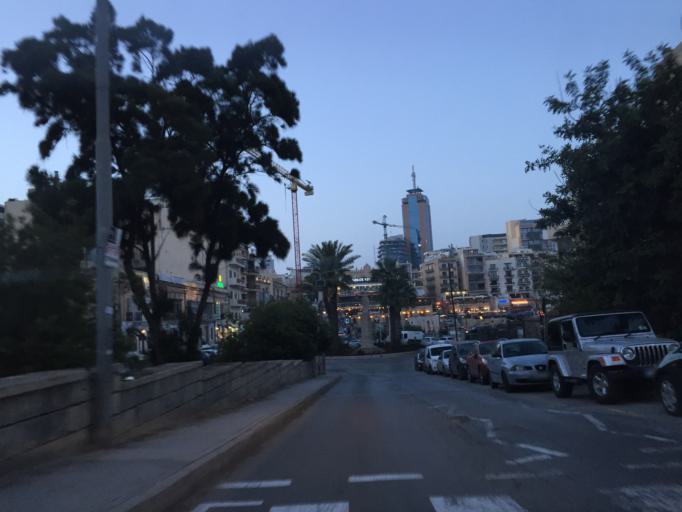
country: MT
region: Saint Julian
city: San Giljan
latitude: 35.9181
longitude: 14.4894
